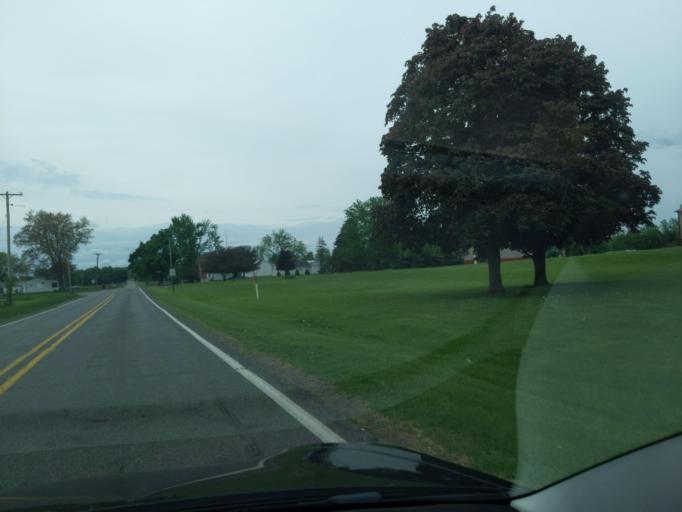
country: US
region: Michigan
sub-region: Ingham County
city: Mason
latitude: 42.5450
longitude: -84.4233
